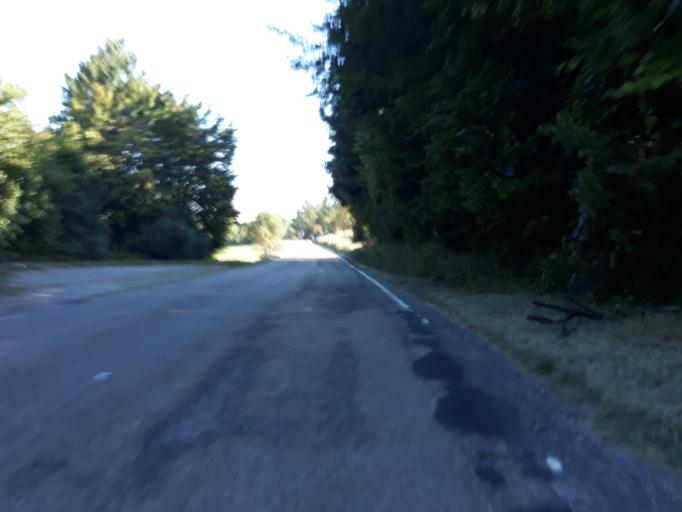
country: DE
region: Baden-Wuerttemberg
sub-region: Regierungsbezirk Stuttgart
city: Aidlingen
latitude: 48.6982
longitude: 8.8951
